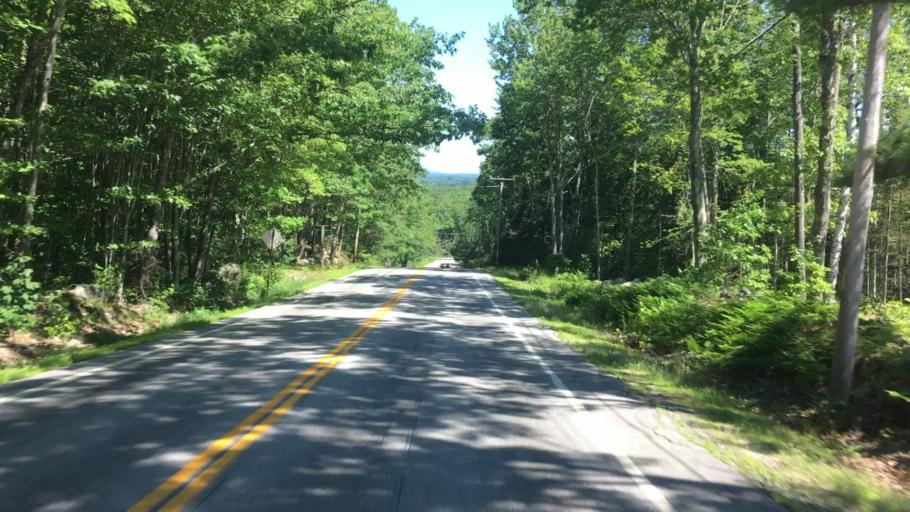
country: US
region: Maine
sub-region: Hancock County
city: Sedgwick
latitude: 44.3439
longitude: -68.6736
